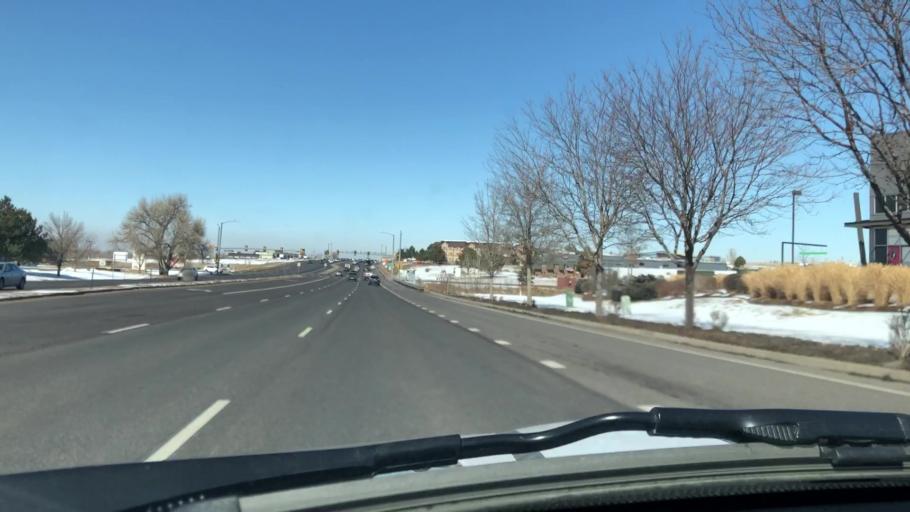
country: US
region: Colorado
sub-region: Douglas County
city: Parker
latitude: 39.5389
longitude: -104.7688
